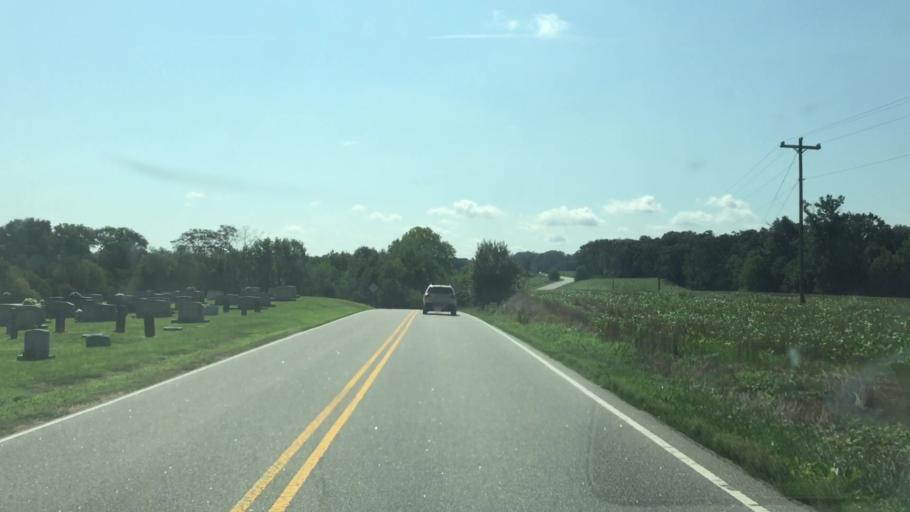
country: US
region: North Carolina
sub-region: Anson County
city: Burnsville
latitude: 35.1030
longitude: -80.3179
